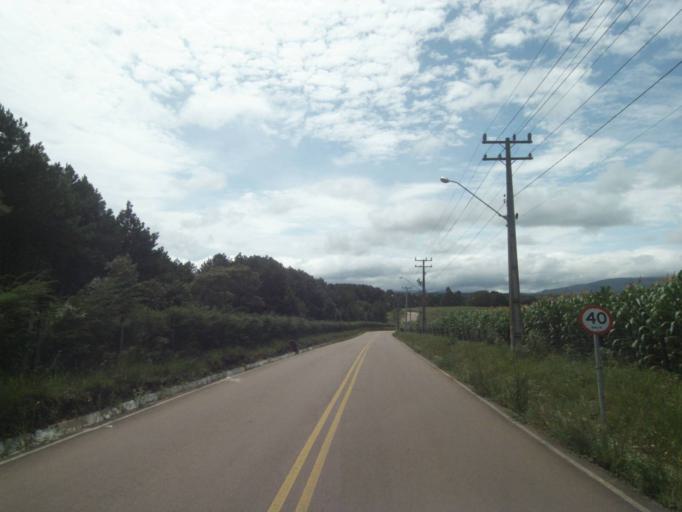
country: BR
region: Parana
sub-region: Campina Grande Do Sul
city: Campina Grande do Sul
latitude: -25.3132
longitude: -49.0313
